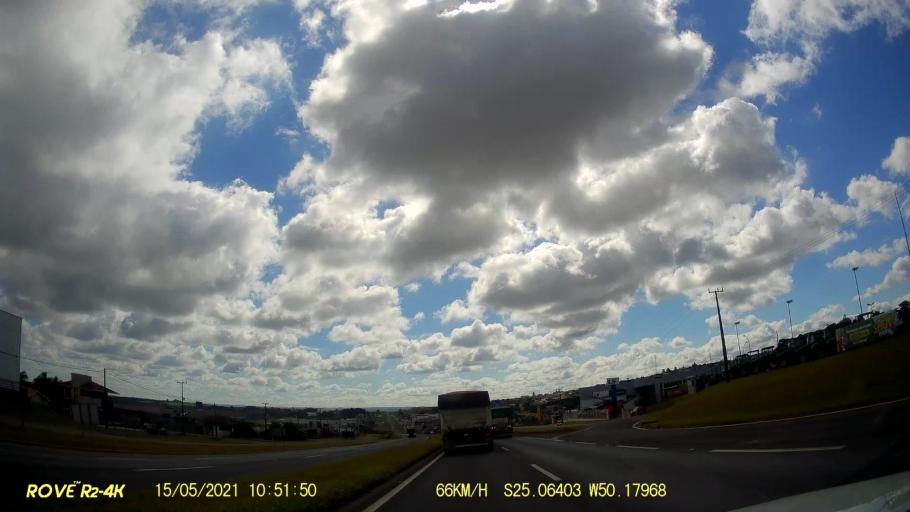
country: BR
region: Parana
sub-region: Ponta Grossa
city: Ponta Grossa
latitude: -25.0641
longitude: -50.1797
